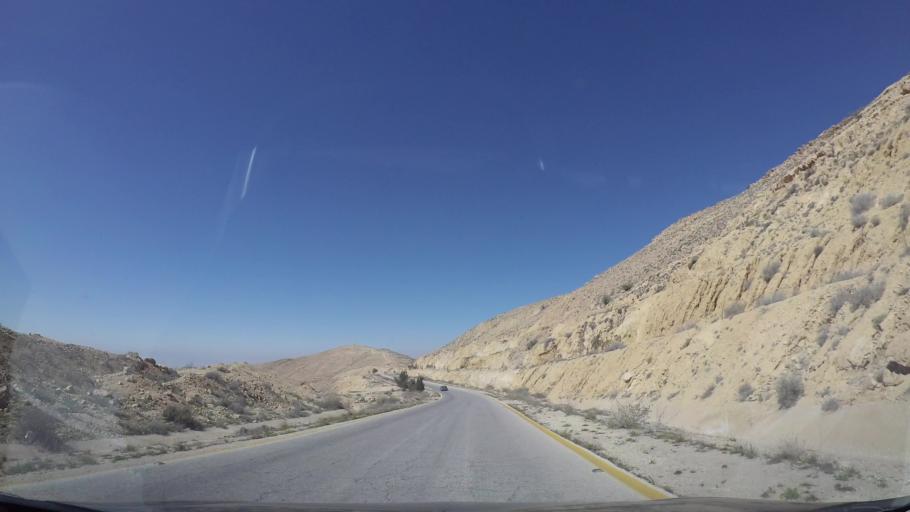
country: JO
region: Tafielah
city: At Tafilah
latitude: 30.8561
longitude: 35.5489
